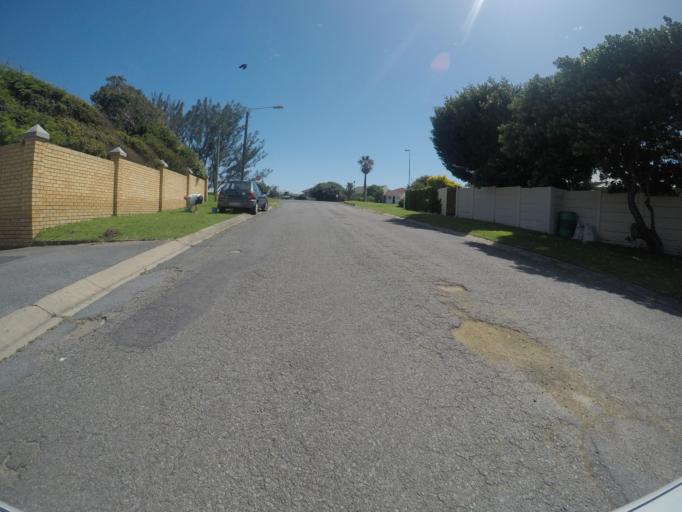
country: ZA
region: Eastern Cape
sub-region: Buffalo City Metropolitan Municipality
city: East London
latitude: -32.9413
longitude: 28.0275
